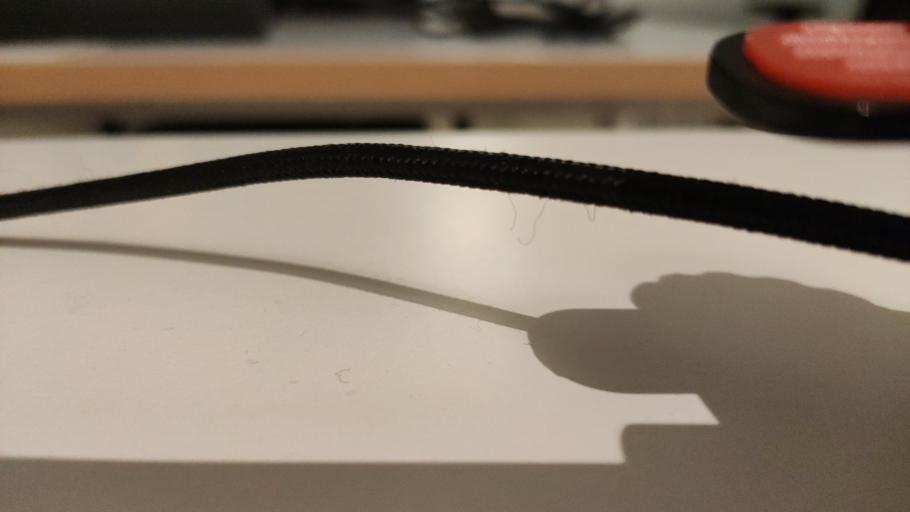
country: RU
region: Moskovskaya
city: Rogachevo
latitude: 56.4347
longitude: 37.1806
